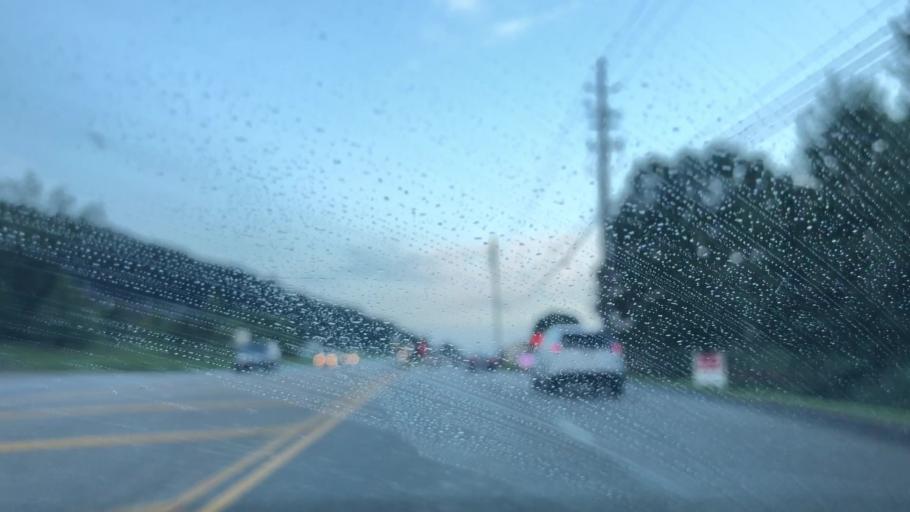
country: US
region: Alabama
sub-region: Shelby County
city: Indian Springs Village
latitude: 33.3617
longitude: -86.7683
